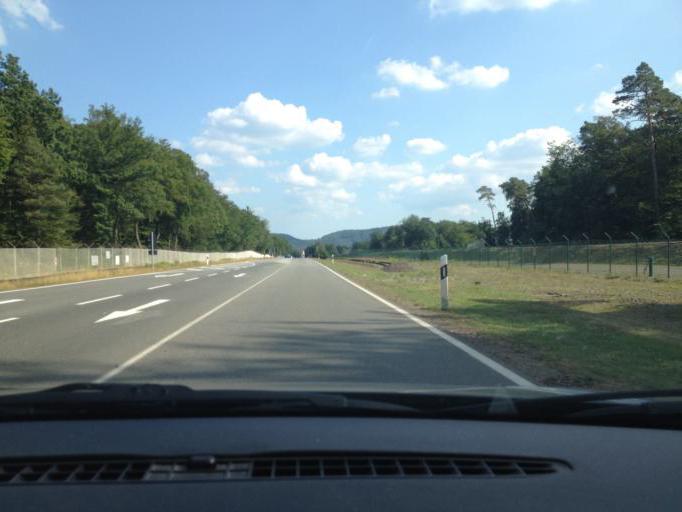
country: DE
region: Rheinland-Pfalz
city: Kindsbach
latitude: 49.4480
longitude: 7.6160
